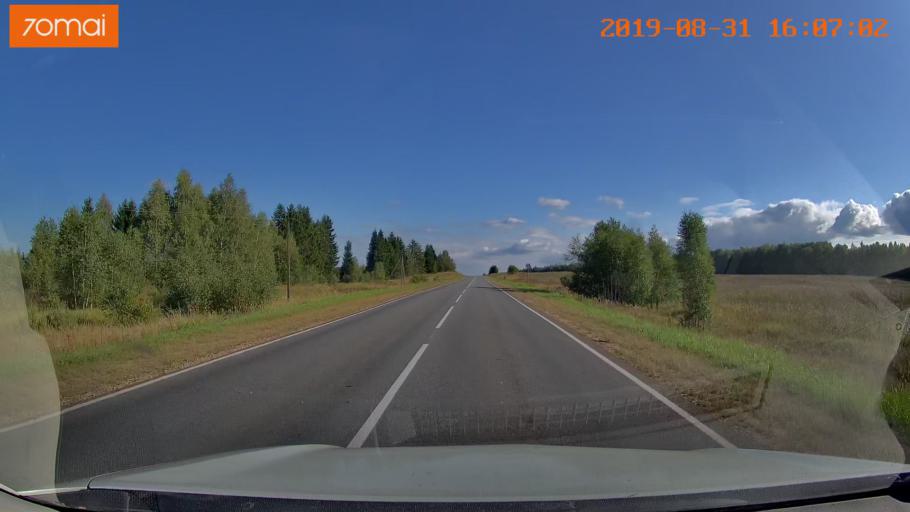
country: RU
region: Kaluga
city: Yukhnov
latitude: 54.6155
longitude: 35.3536
